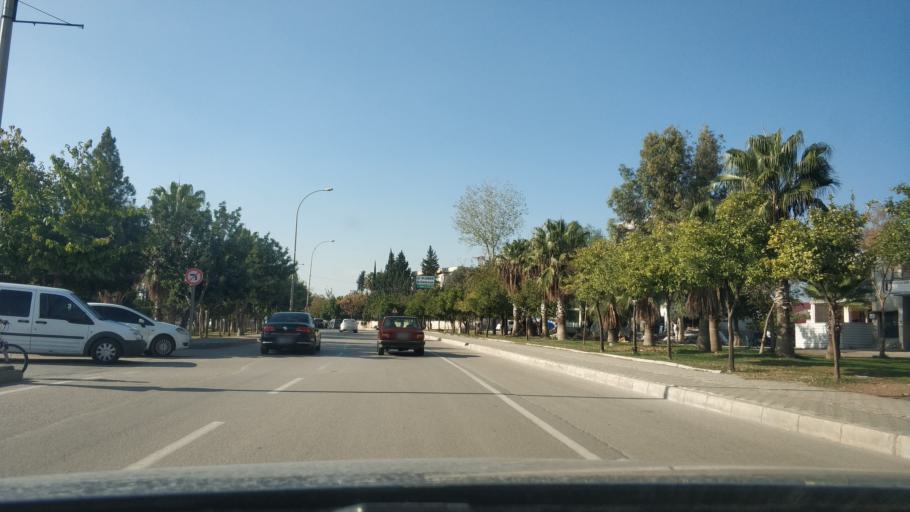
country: TR
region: Adana
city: Seyhan
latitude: 37.0119
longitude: 35.2833
